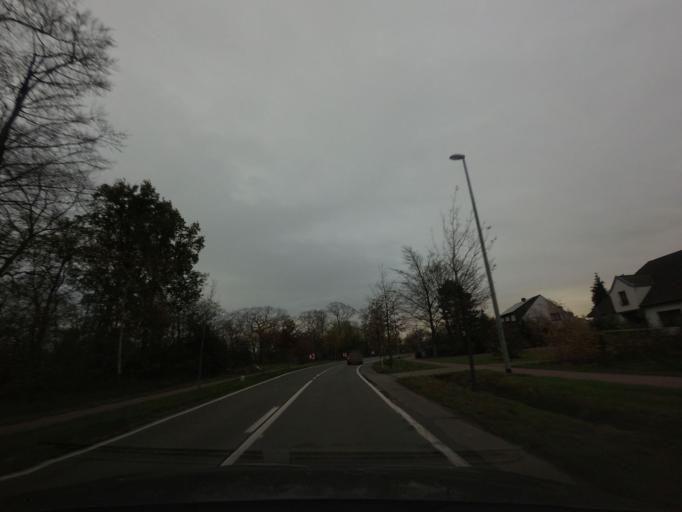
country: BE
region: Flanders
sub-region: Provincie Antwerpen
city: Brecht
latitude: 51.3378
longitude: 4.6182
